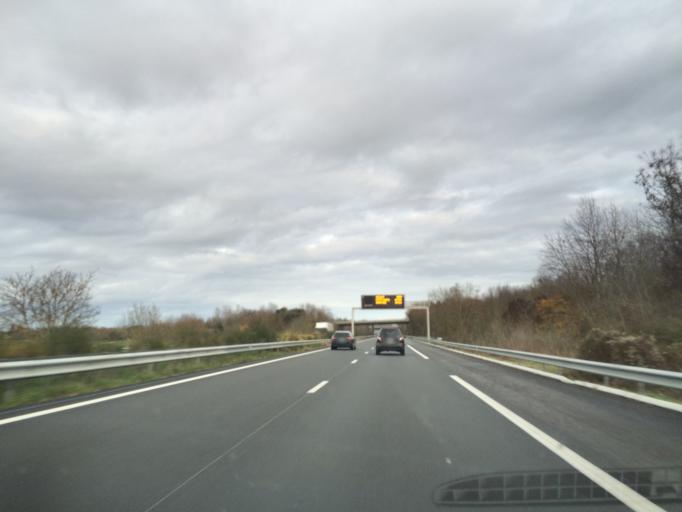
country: FR
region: Poitou-Charentes
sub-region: Departement des Deux-Sevres
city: Beauvoir-sur-Niort
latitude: 46.2039
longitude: -0.4720
